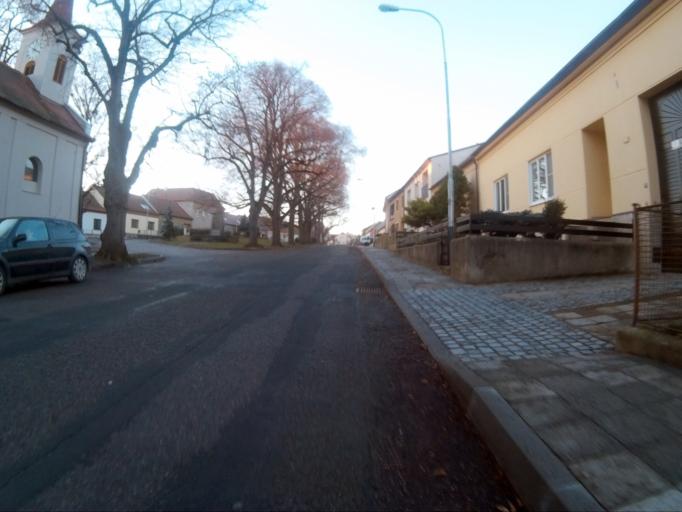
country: CZ
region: South Moravian
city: Troubsko
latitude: 49.1761
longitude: 16.5299
